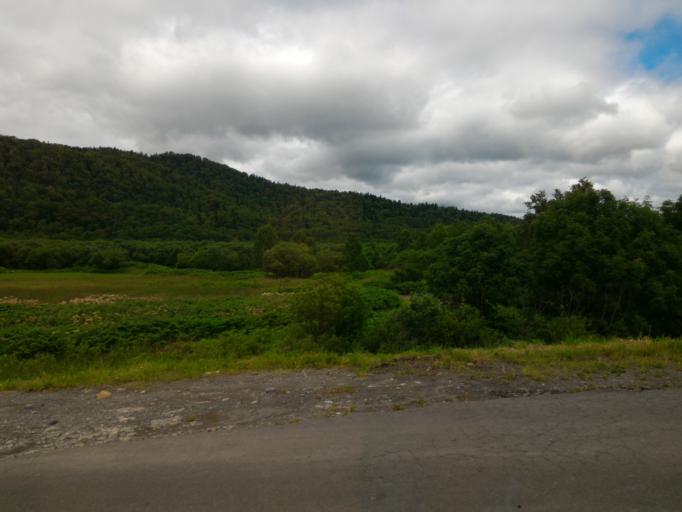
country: JP
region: Hokkaido
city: Nayoro
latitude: 44.7255
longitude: 142.2529
